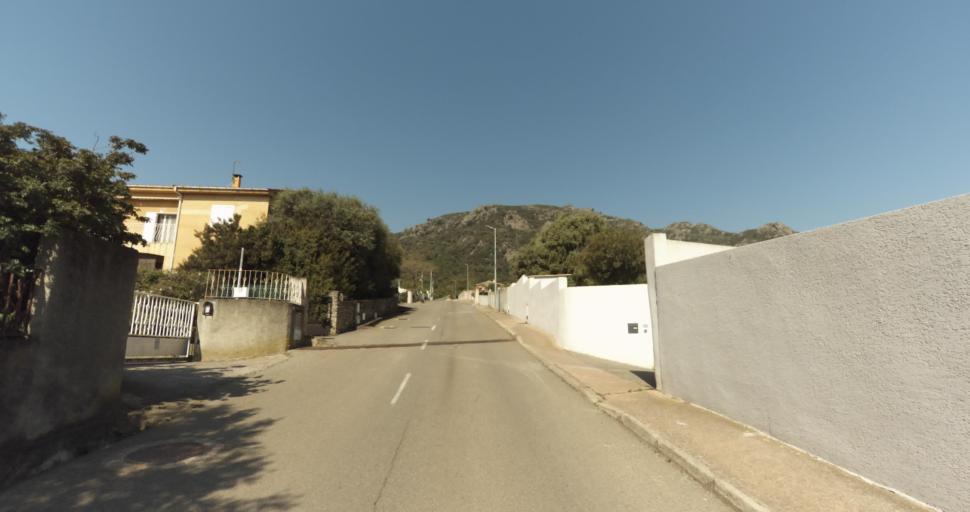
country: FR
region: Corsica
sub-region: Departement de la Haute-Corse
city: Biguglia
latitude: 42.6221
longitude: 9.4256
